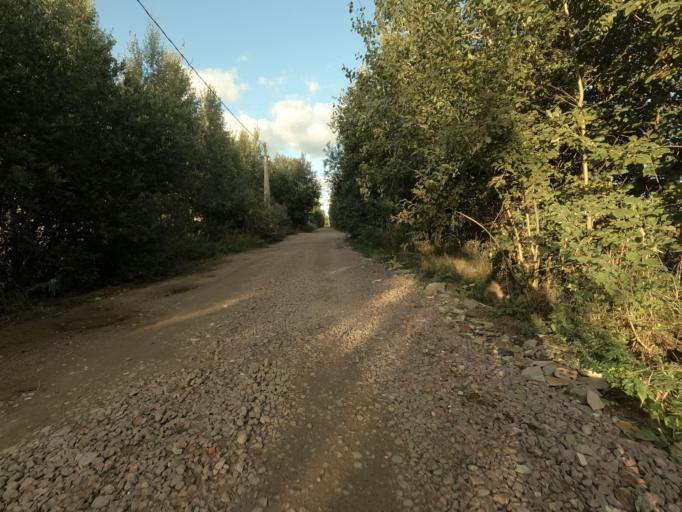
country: RU
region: Leningrad
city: Otradnoye
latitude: 59.8679
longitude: 30.7698
